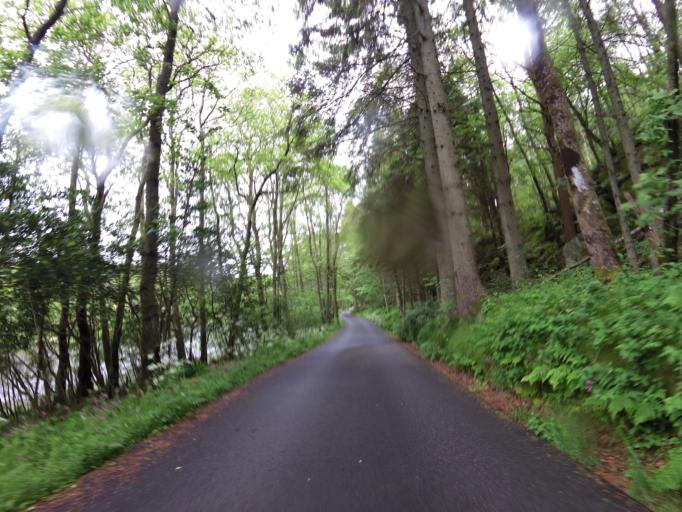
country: NO
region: Vest-Agder
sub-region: Mandal
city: Mandal
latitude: 58.0112
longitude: 7.5192
